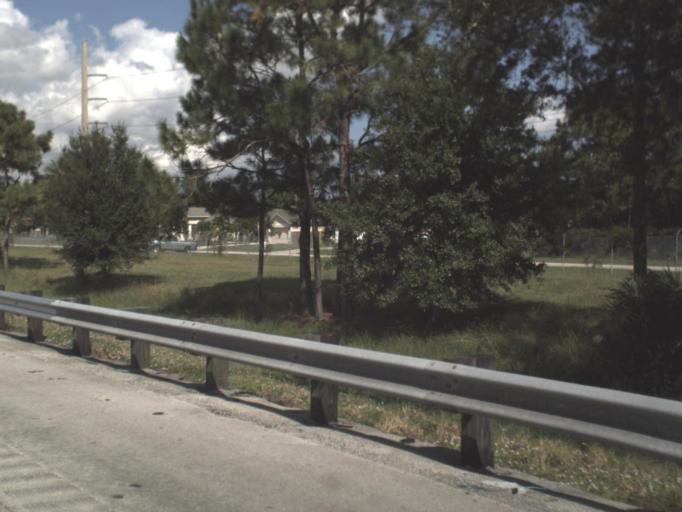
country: US
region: Florida
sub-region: Saint Lucie County
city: Port Saint Lucie
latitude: 27.2660
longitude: -80.3542
